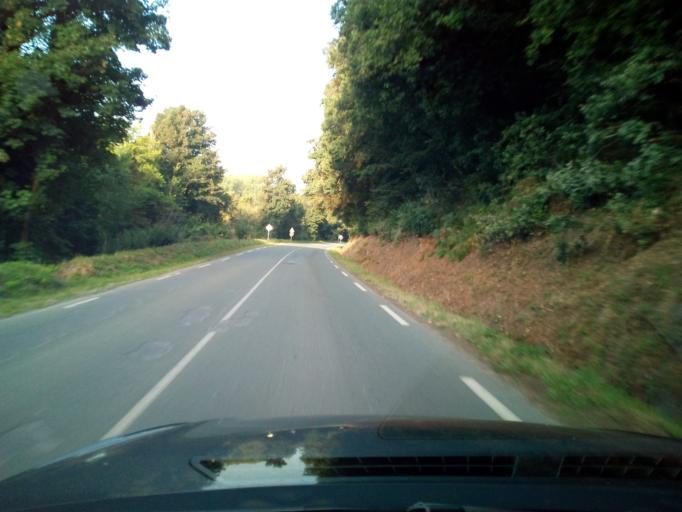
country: FR
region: Brittany
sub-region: Departement du Finistere
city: La Roche-Maurice
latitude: 48.4898
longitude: -4.1563
